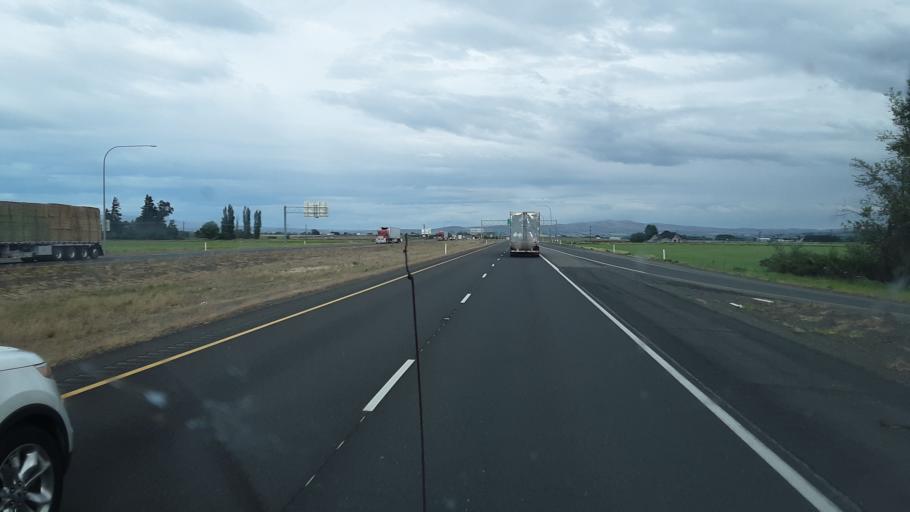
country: US
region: Washington
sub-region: Kittitas County
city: Ellensburg
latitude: 46.9719
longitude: -120.5343
